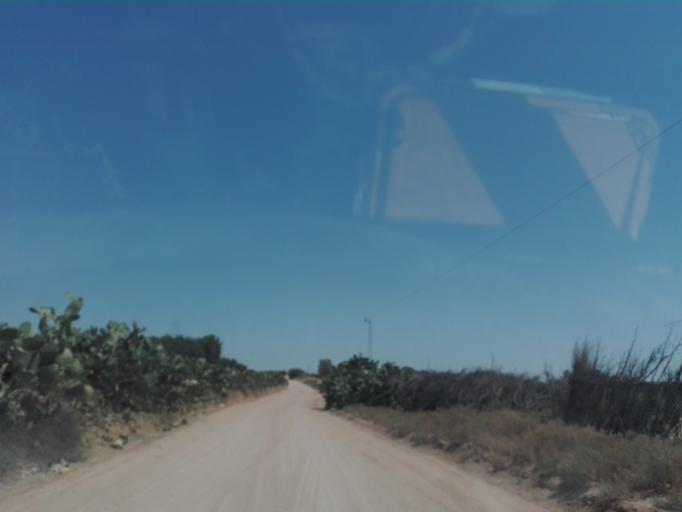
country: TN
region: Safaqis
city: Bi'r `Ali Bin Khalifah
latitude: 34.6623
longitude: 10.2399
